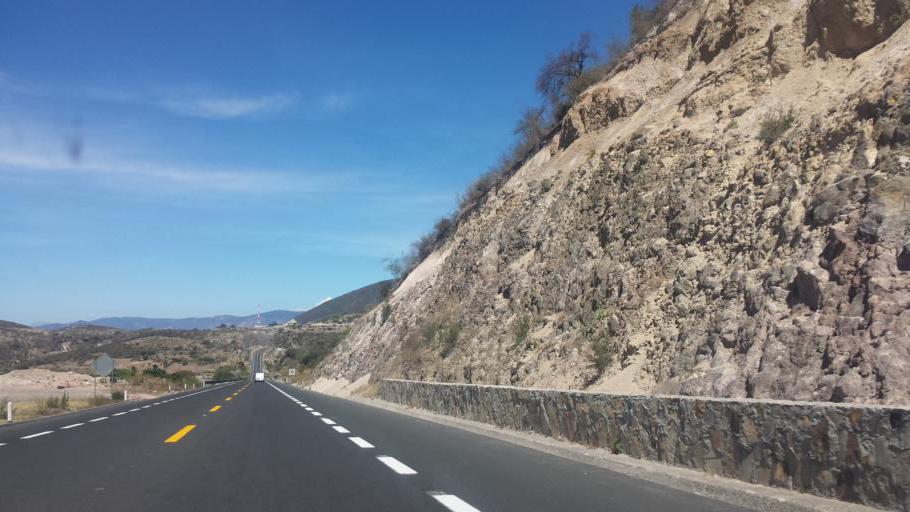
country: MX
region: Oaxaca
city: San Gabriel Casa Blanca
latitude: 17.9650
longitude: -97.3575
